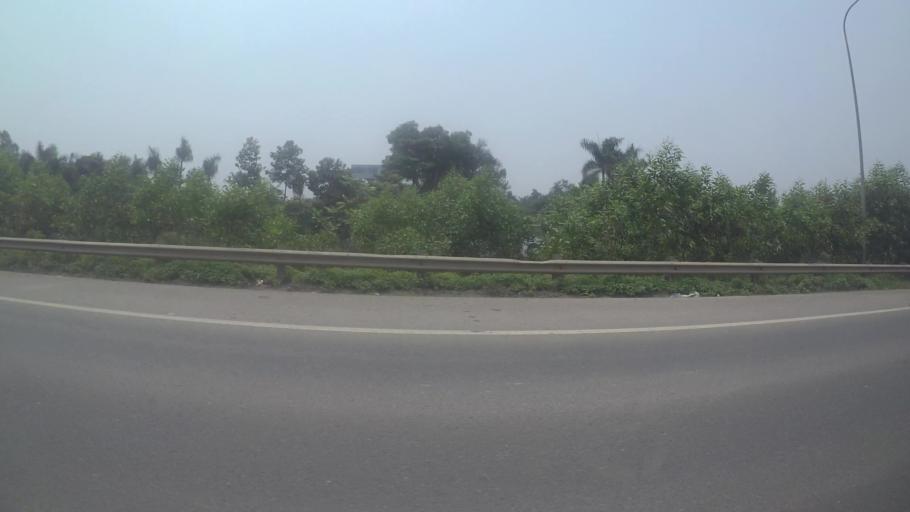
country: VN
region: Ha Noi
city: Lien Quan
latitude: 20.9897
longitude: 105.5590
